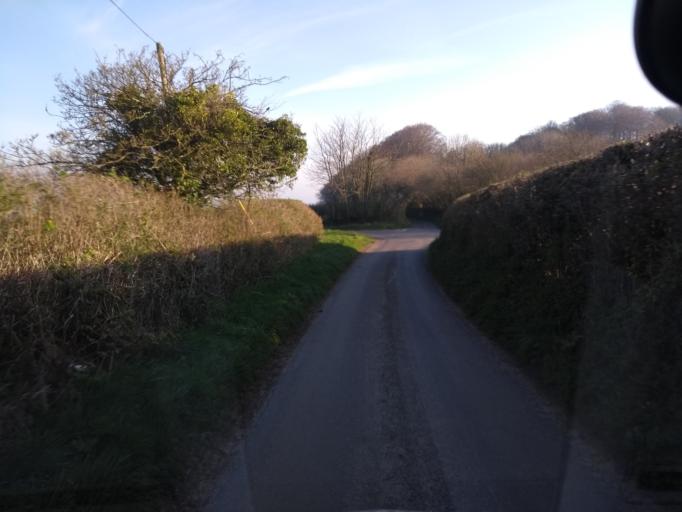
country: GB
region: England
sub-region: Somerset
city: Crewkerne
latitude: 50.8653
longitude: -2.8064
